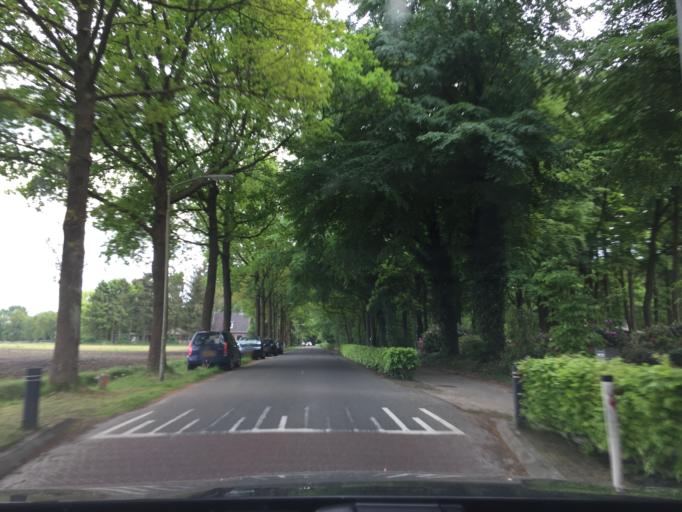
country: NL
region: Drenthe
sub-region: Gemeente Tynaarlo
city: Tynaarlo
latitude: 53.0736
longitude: 6.6323
